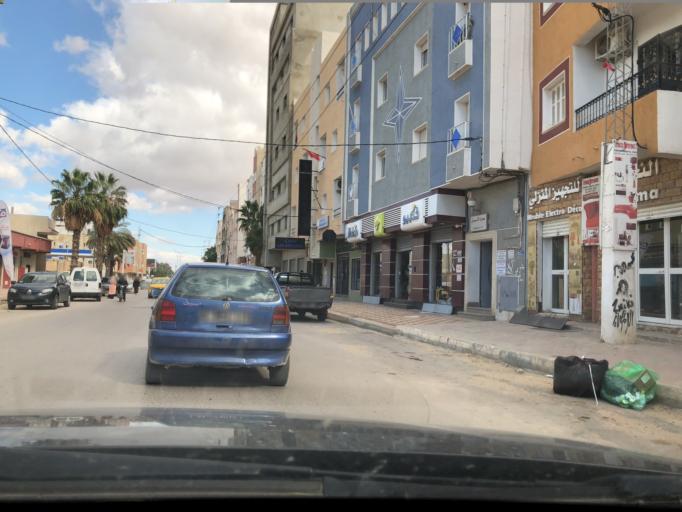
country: TN
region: Al Qasrayn
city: Kasserine
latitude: 35.1706
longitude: 8.8396
